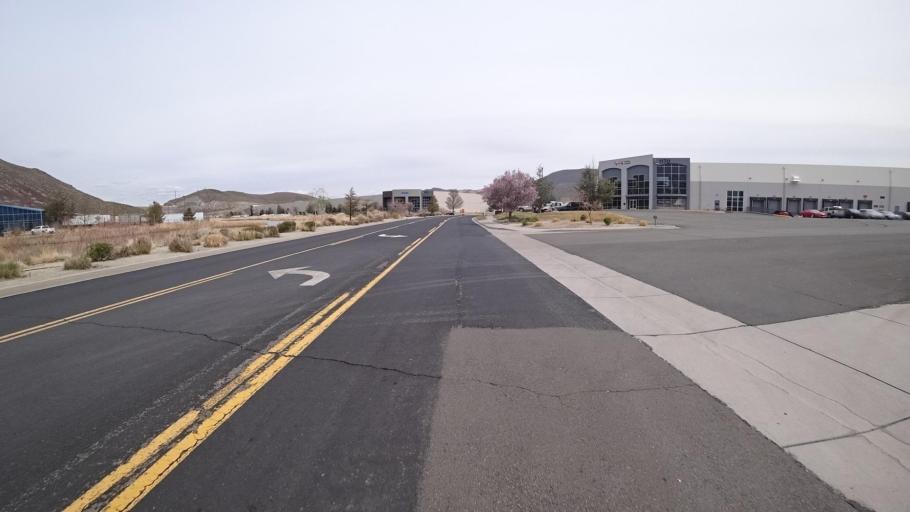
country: US
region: Nevada
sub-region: Washoe County
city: Sparks
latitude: 39.4514
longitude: -119.7458
